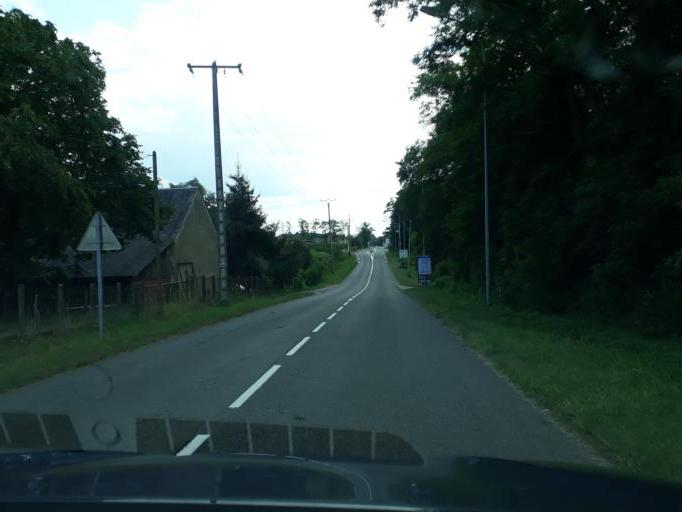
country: FR
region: Centre
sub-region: Departement du Cher
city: Jouet-sur-l'Aubois
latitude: 46.9611
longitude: 2.9593
